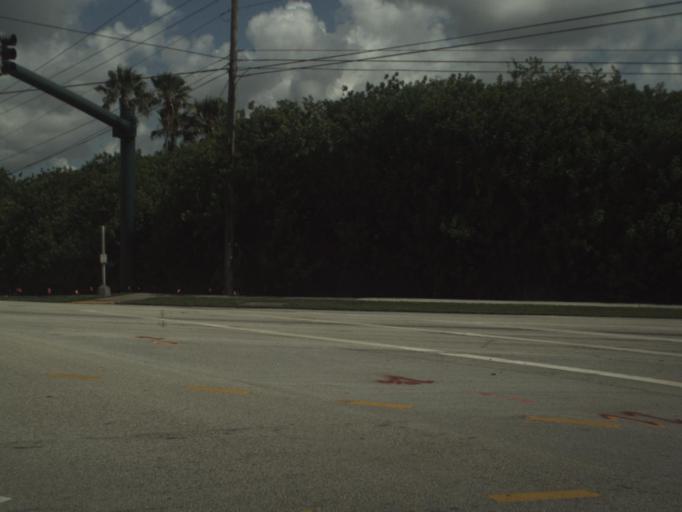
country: US
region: Florida
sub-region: Palm Beach County
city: Palm Beach Gardens
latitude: 26.8102
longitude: -80.1525
